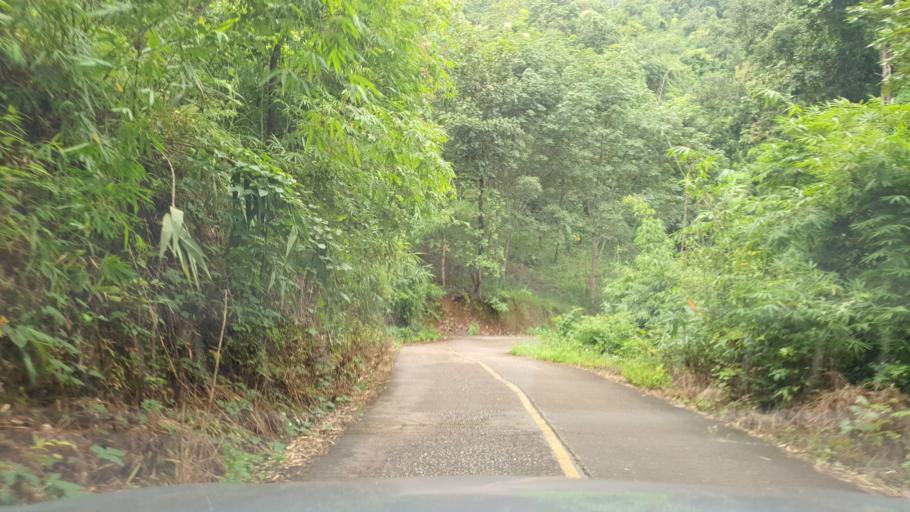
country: TH
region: Chiang Mai
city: Mae Taeng
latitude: 19.2219
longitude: 98.9247
